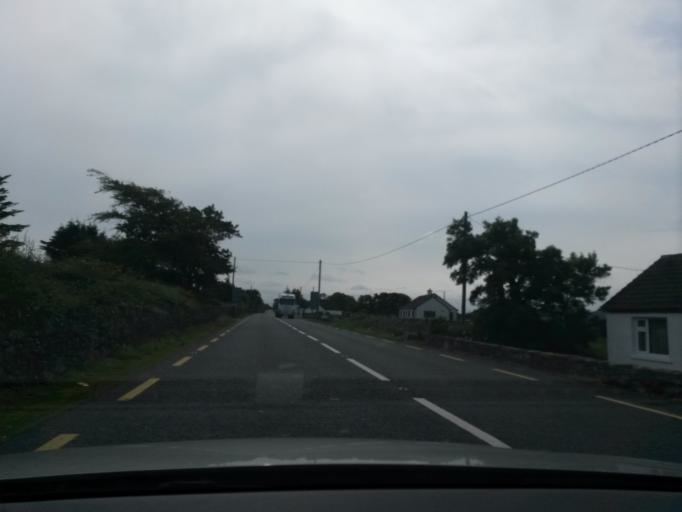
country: IE
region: Connaught
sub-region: Sligo
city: Sligo
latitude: 54.4280
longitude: -8.4591
